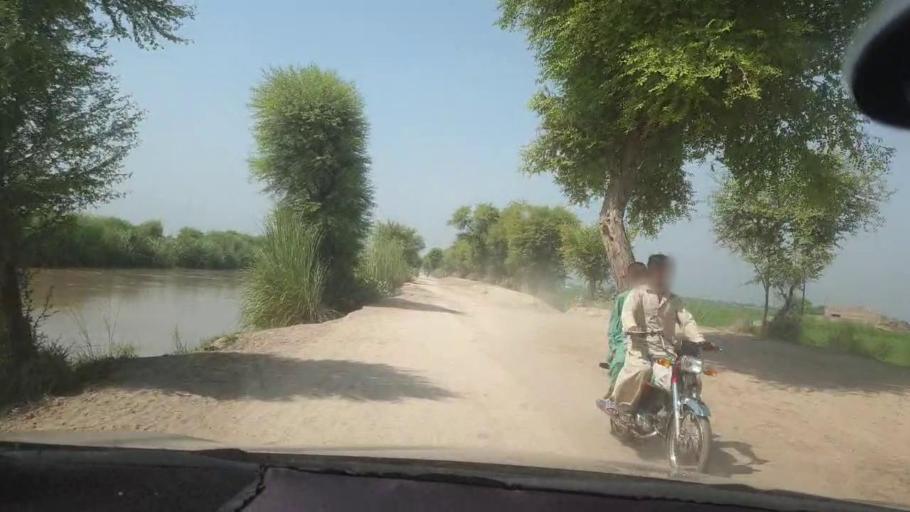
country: PK
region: Sindh
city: Shahdadkot
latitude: 27.7250
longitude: 67.9574
